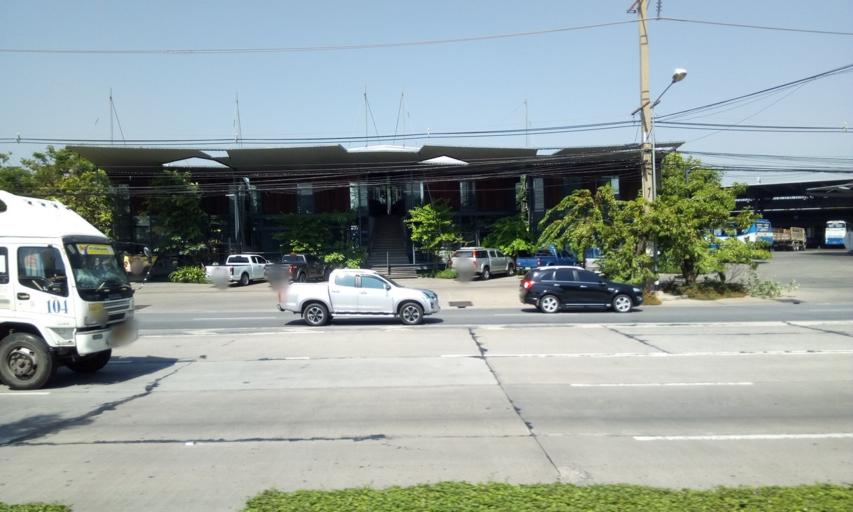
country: TH
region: Nakhon Ratchasima
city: Nakhon Ratchasima
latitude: 14.9616
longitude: 102.0625
